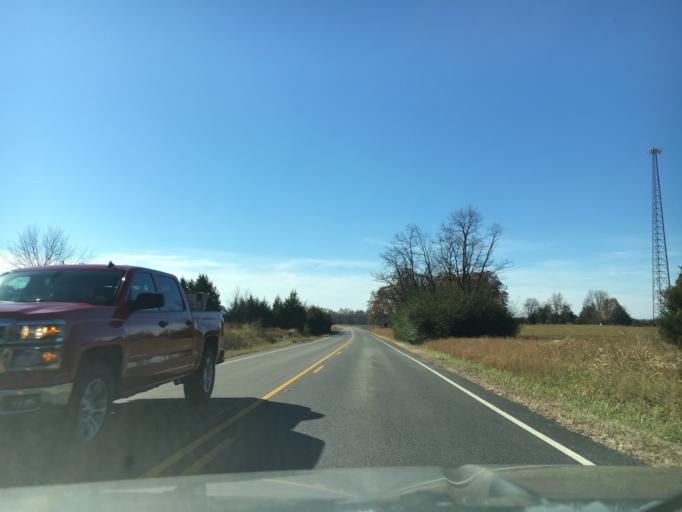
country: US
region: Virginia
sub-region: Cumberland County
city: Cumberland
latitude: 37.5667
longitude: -78.1816
